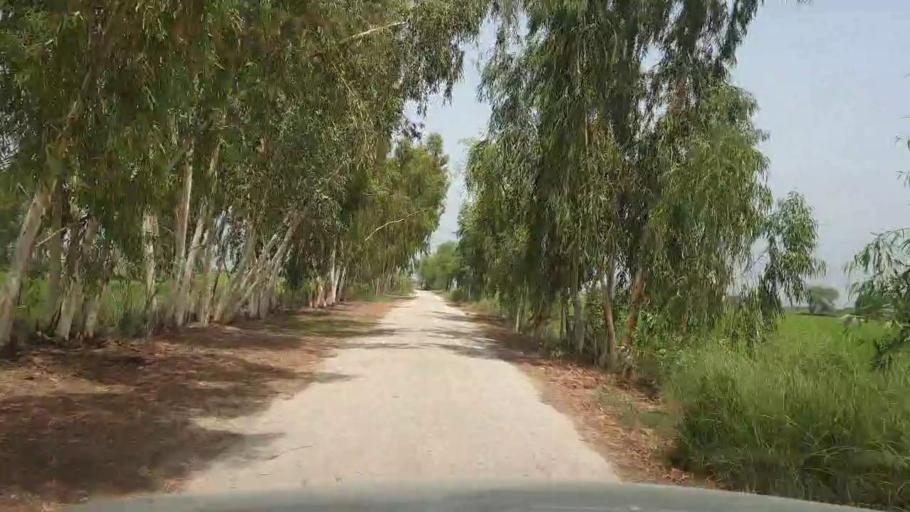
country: PK
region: Sindh
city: Garhi Yasin
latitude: 27.9476
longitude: 68.3684
